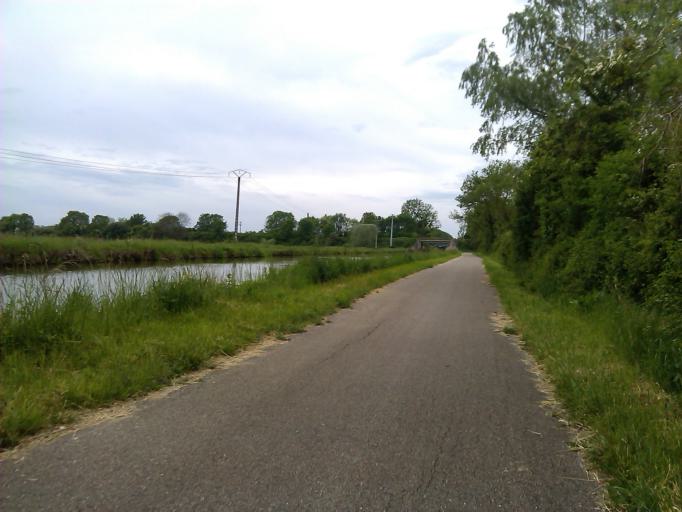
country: FR
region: Franche-Comte
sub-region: Departement du Jura
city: Damparis
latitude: 47.0597
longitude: 5.4332
